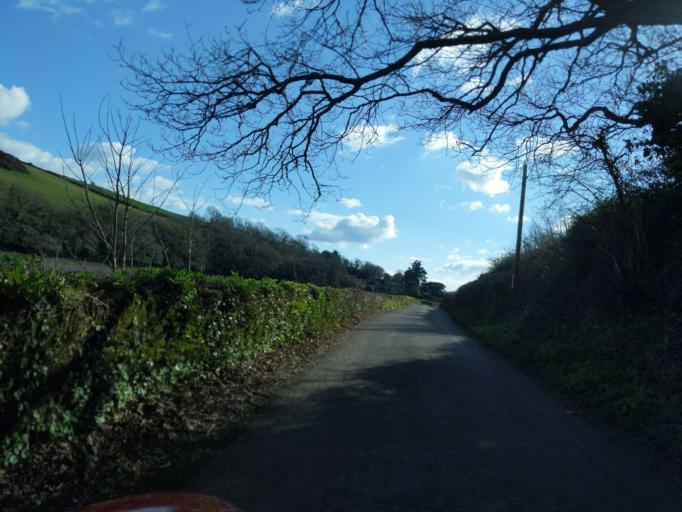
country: GB
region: England
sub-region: Devon
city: Kingsbridge
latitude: 50.2778
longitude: -3.7611
